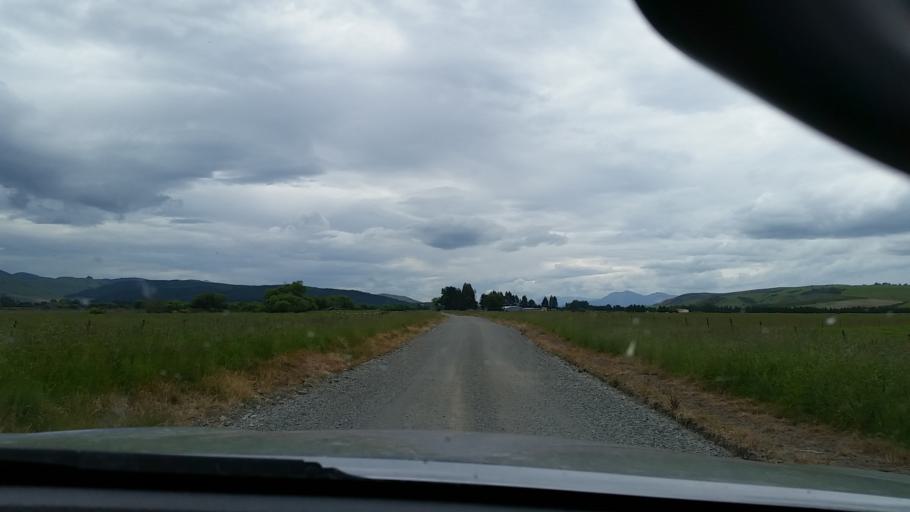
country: NZ
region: Southland
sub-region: Southland District
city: Winton
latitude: -45.8592
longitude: 168.1376
